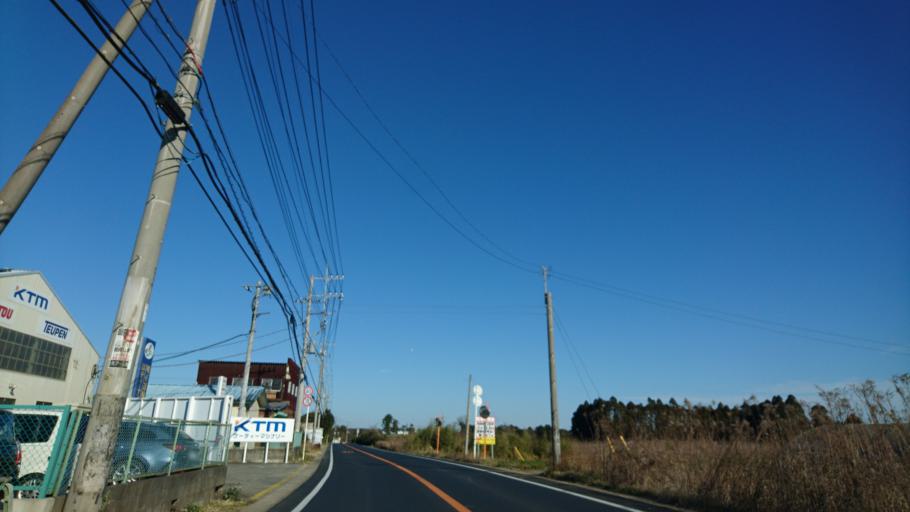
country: JP
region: Chiba
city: Yachimata
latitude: 35.5953
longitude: 140.3202
